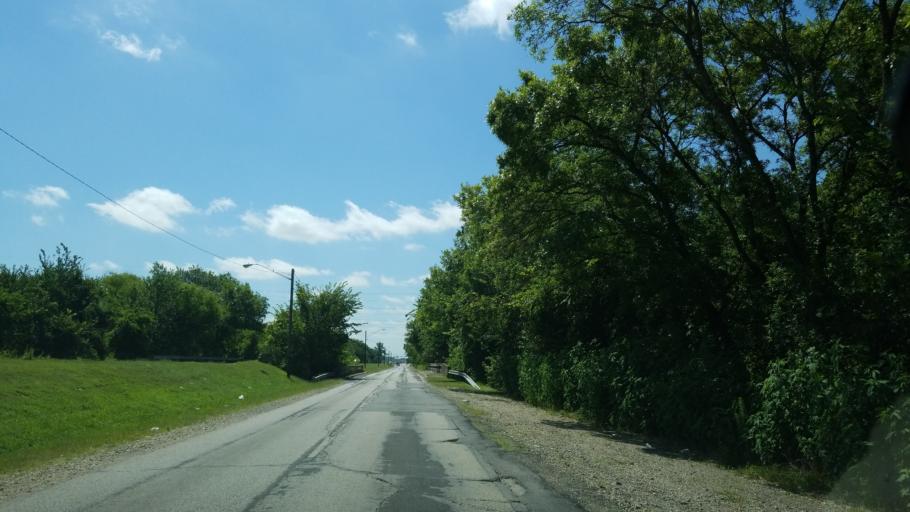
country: US
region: Texas
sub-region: Dallas County
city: Dallas
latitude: 32.7515
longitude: -96.7335
